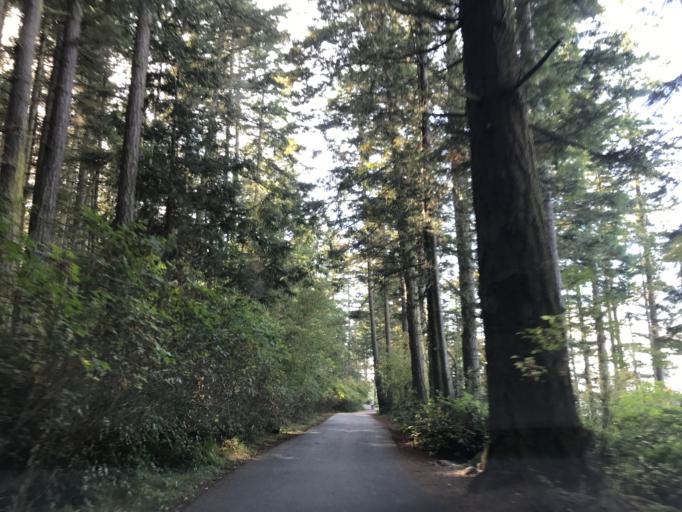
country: US
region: Washington
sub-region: Skagit County
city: Anacortes
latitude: 48.4997
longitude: -122.6951
